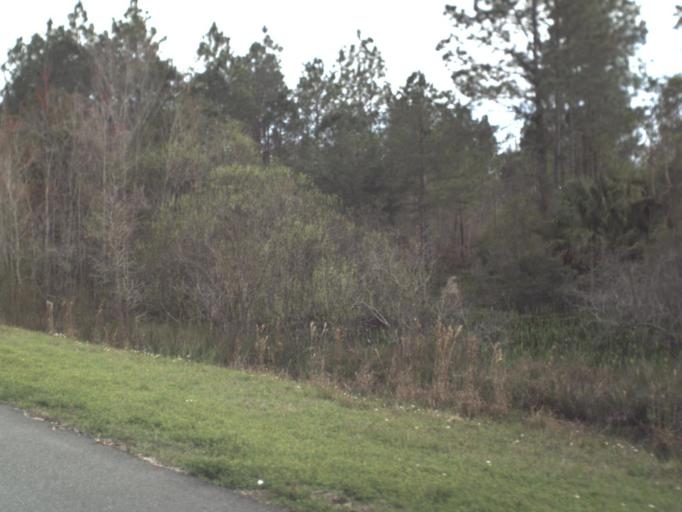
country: US
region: Florida
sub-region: Leon County
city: Woodville
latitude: 30.1831
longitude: -84.0146
